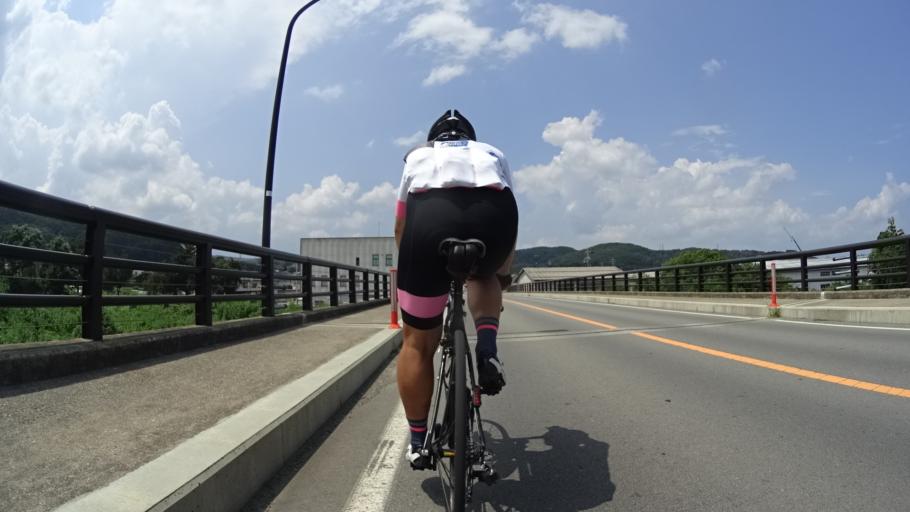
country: JP
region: Nagano
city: Saku
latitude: 36.1583
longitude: 138.4833
